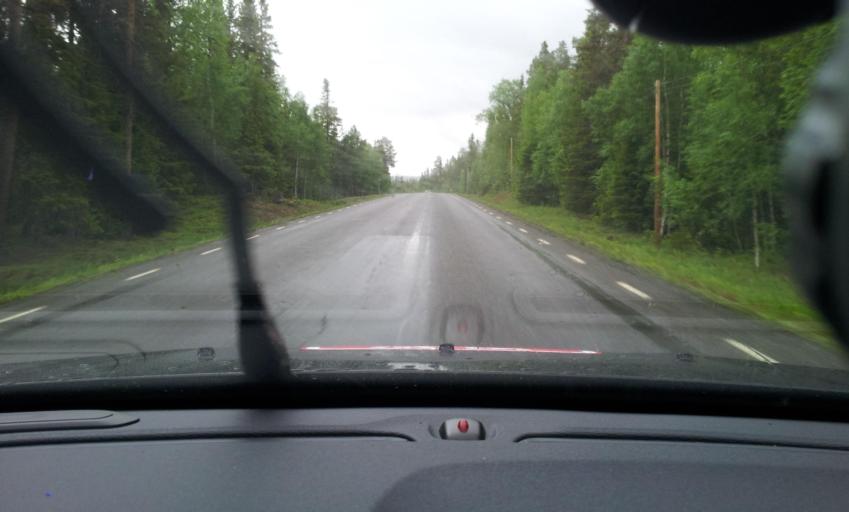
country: SE
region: Jaemtland
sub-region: Are Kommun
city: Are
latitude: 63.2134
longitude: 13.1612
